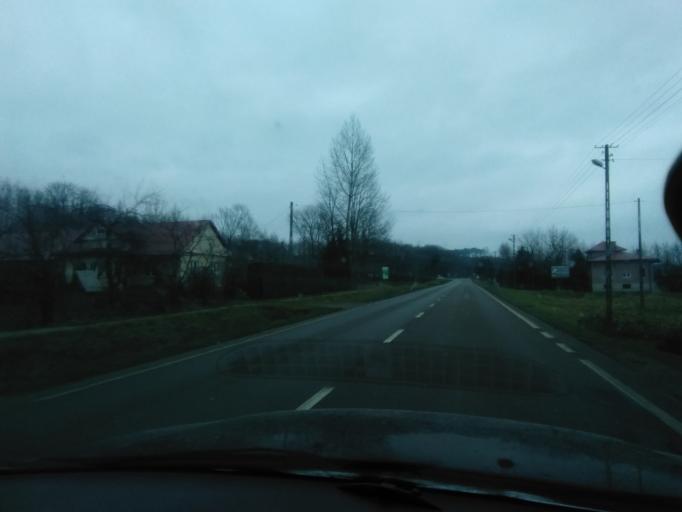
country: PL
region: Subcarpathian Voivodeship
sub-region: Powiat rzeszowski
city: Dynow
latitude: 49.8349
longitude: 22.2846
